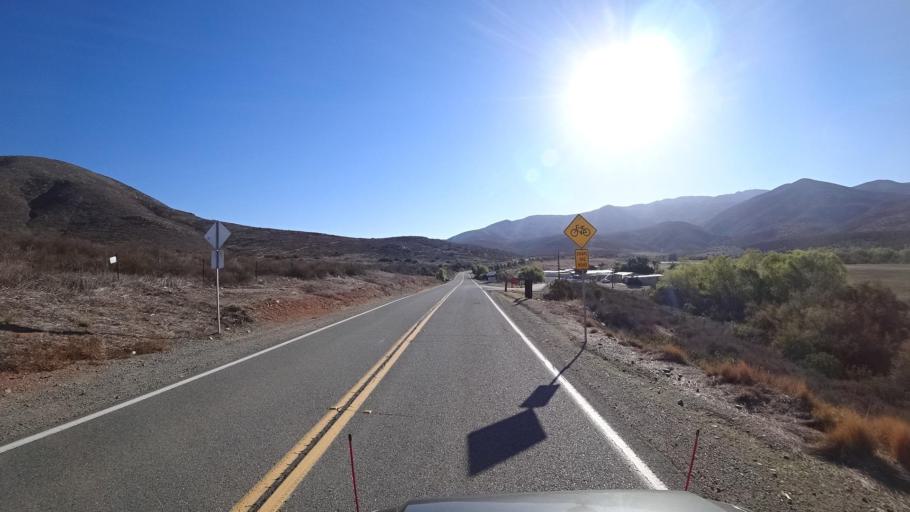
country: US
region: California
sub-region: San Diego County
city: Jamul
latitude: 32.6359
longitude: -116.8936
